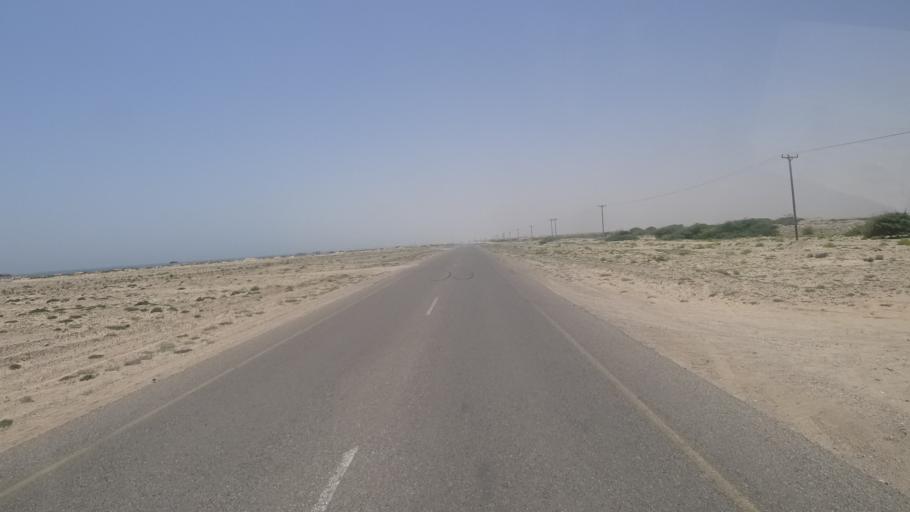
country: OM
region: Ash Sharqiyah
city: Sur
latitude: 22.1019
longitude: 59.7036
